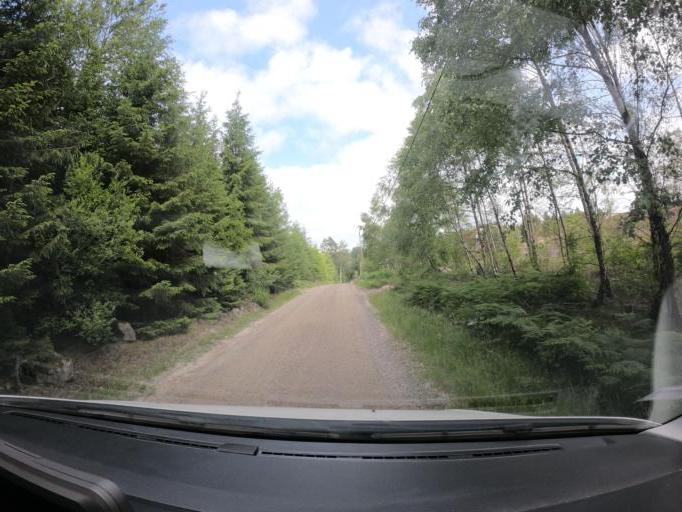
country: SE
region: Skane
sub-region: Hoors Kommun
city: Hoeoer
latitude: 56.0306
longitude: 13.5286
